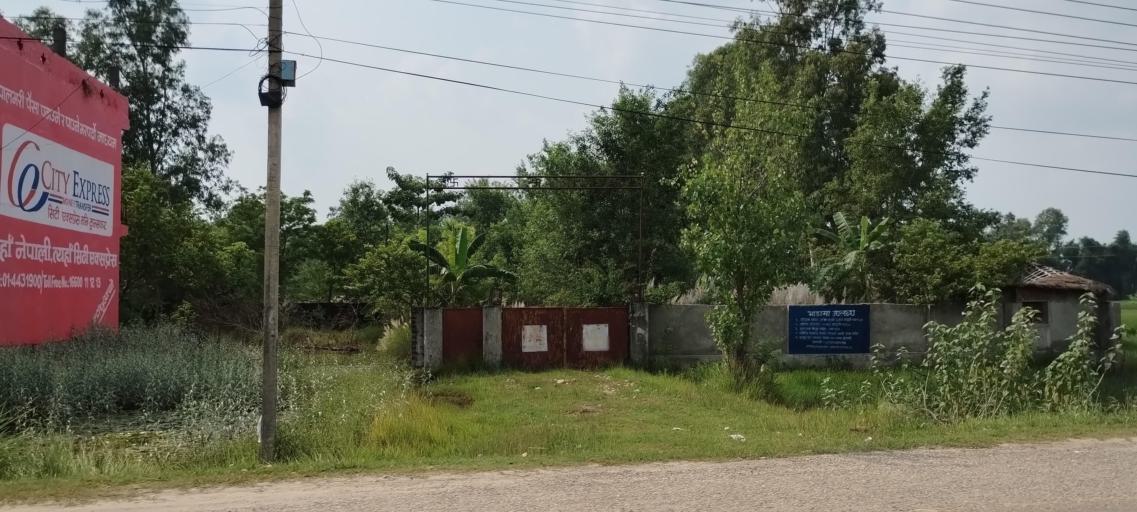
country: NP
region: Mid Western
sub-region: Bheri Zone
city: Nepalgunj
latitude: 28.1682
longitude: 81.6753
